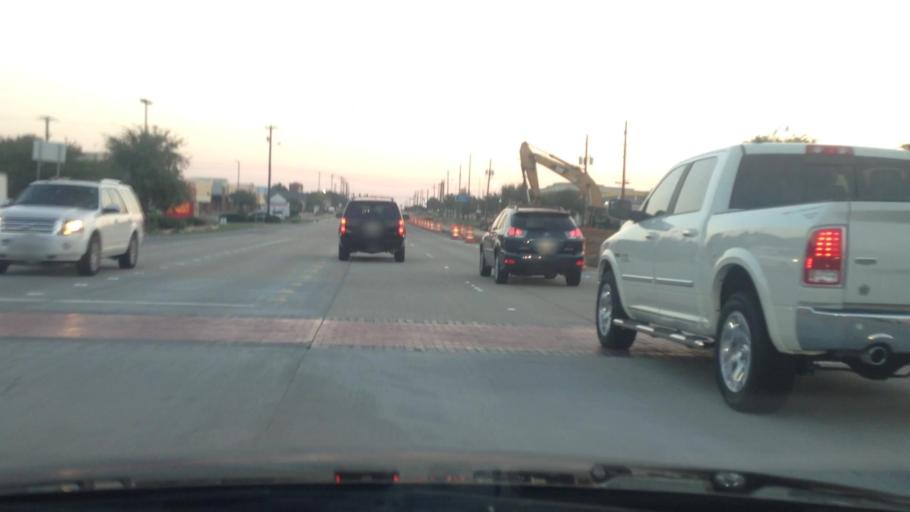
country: US
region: Texas
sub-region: Tarrant County
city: Colleyville
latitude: 32.8890
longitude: -97.1502
